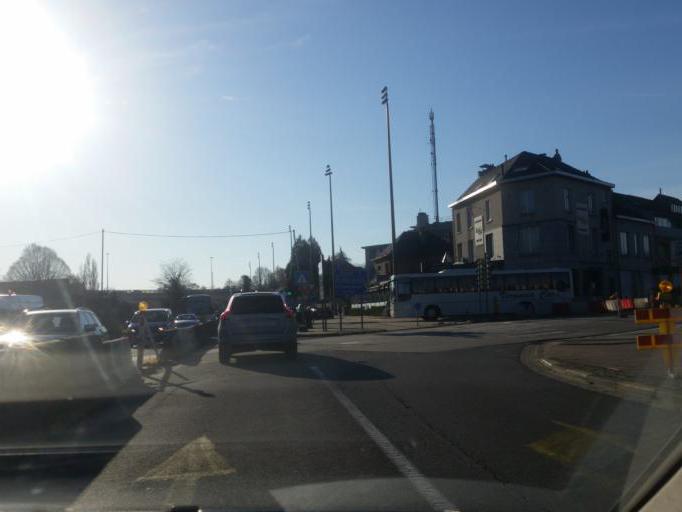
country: BE
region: Flanders
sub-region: Provincie Vlaams-Brabant
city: Kraainem
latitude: 50.8685
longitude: 4.4529
